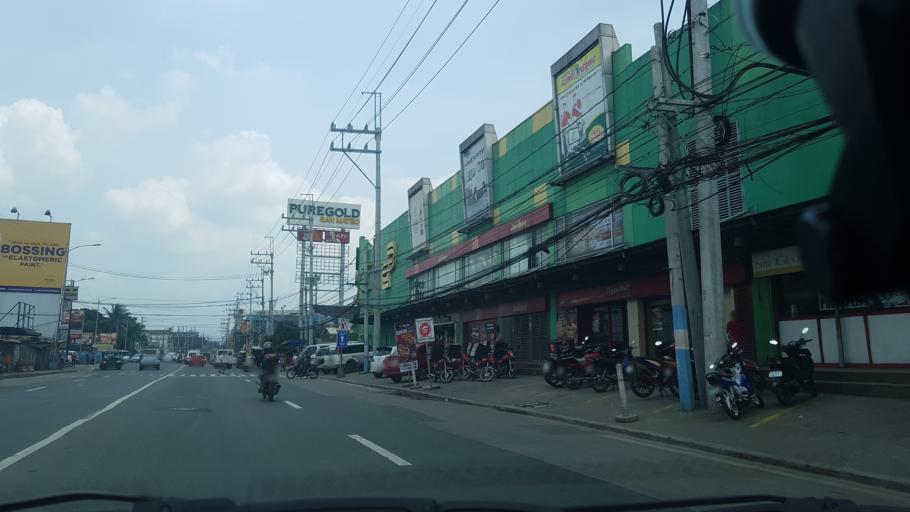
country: PH
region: Calabarzon
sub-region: Province of Rizal
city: San Mateo
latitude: 14.6769
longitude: 121.1110
